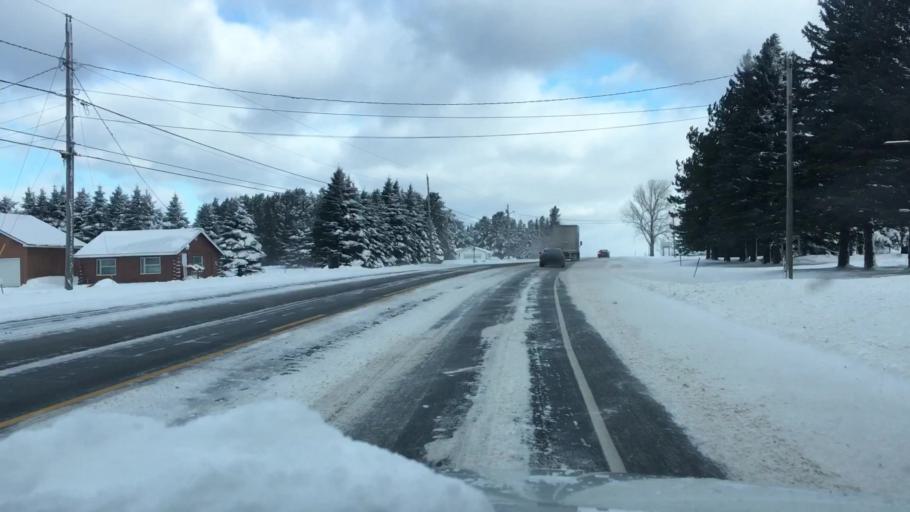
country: US
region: Maine
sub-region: Aroostook County
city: Caribou
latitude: 46.7911
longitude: -67.9914
